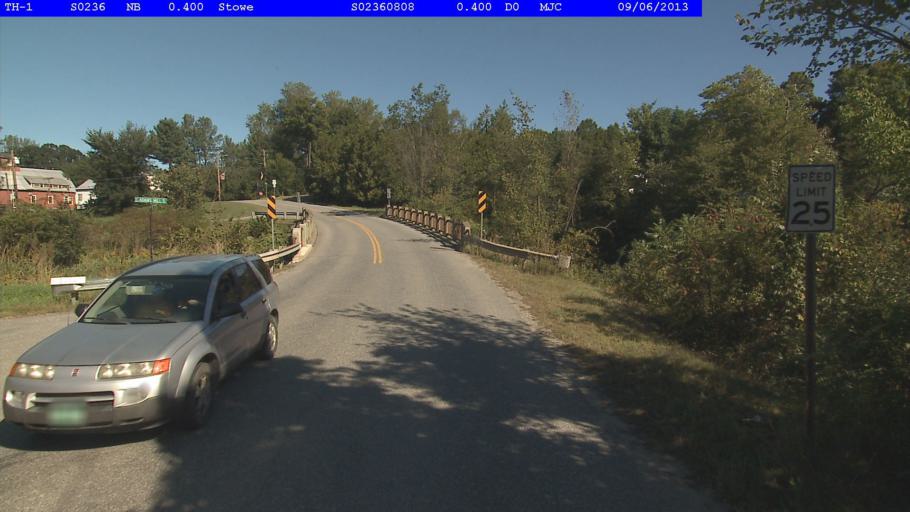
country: US
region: Vermont
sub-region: Washington County
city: Waterbury
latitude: 44.4406
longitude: -72.7147
